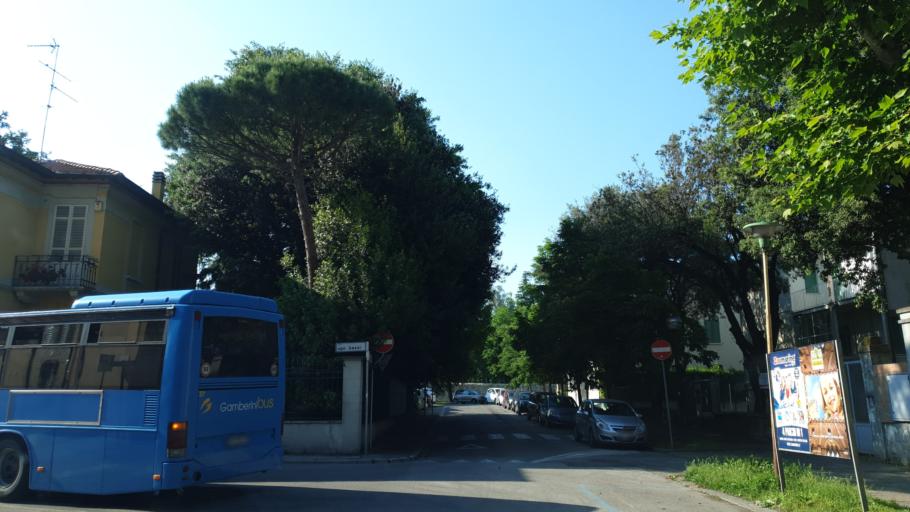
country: IT
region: Emilia-Romagna
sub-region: Provincia di Ravenna
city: Ravenna
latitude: 44.4206
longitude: 12.2069
